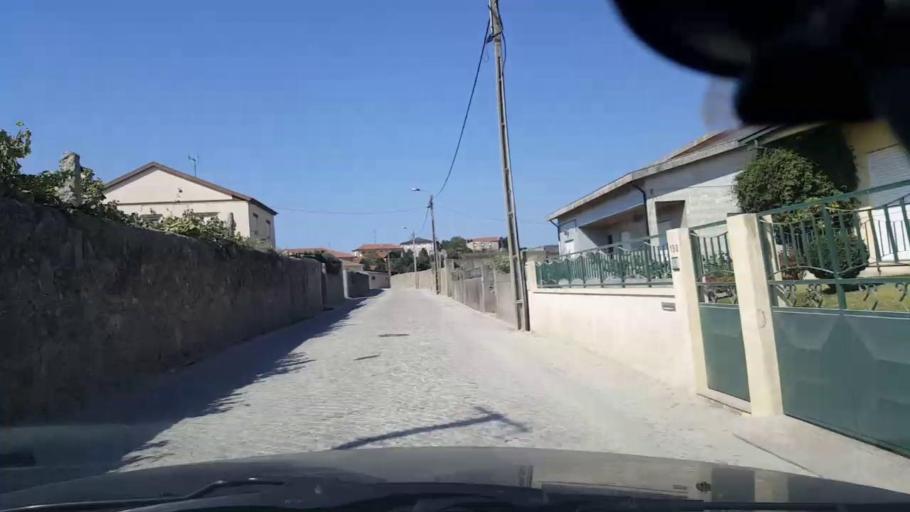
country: PT
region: Porto
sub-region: Povoa de Varzim
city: Pedroso
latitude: 41.3979
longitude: -8.6881
